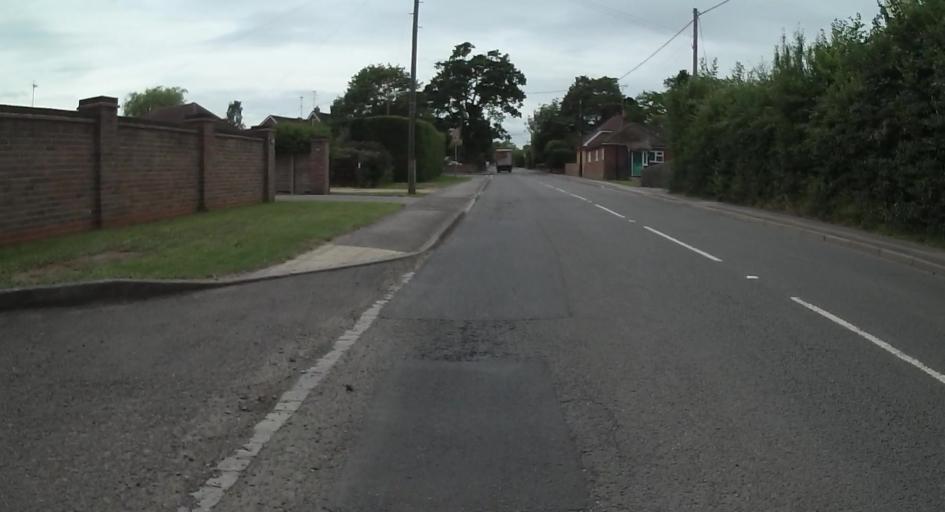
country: GB
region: England
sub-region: Wokingham
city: Swallowfield
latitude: 51.3943
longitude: -0.9666
